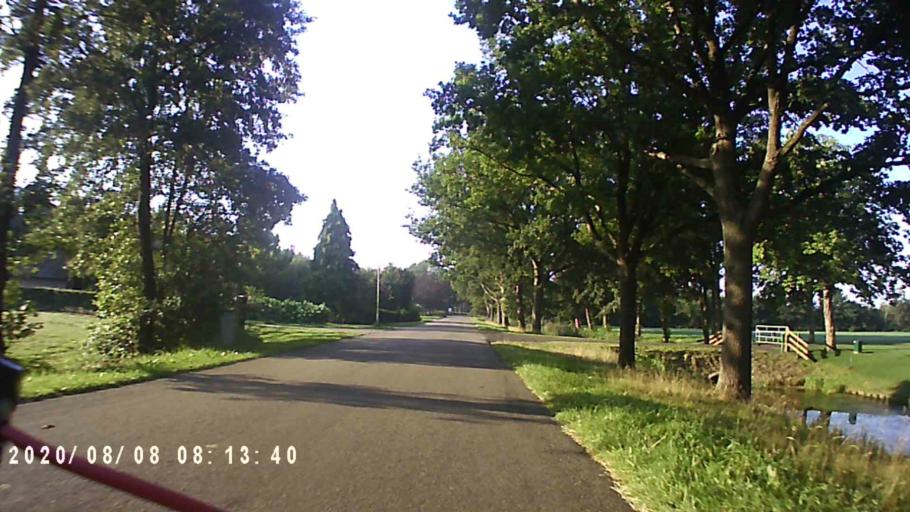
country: NL
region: Groningen
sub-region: Gemeente Leek
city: Leek
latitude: 53.0992
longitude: 6.3405
